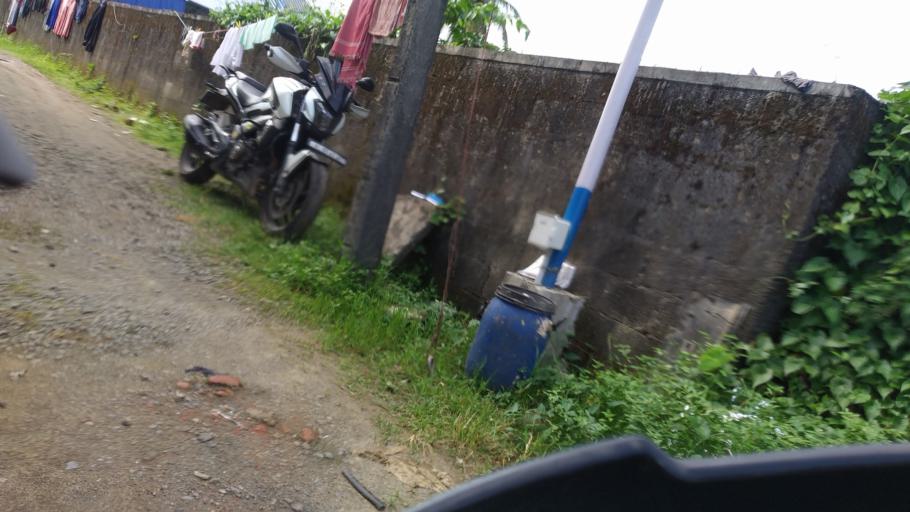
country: IN
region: Kerala
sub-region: Ernakulam
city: Cochin
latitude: 9.9892
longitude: 76.3009
